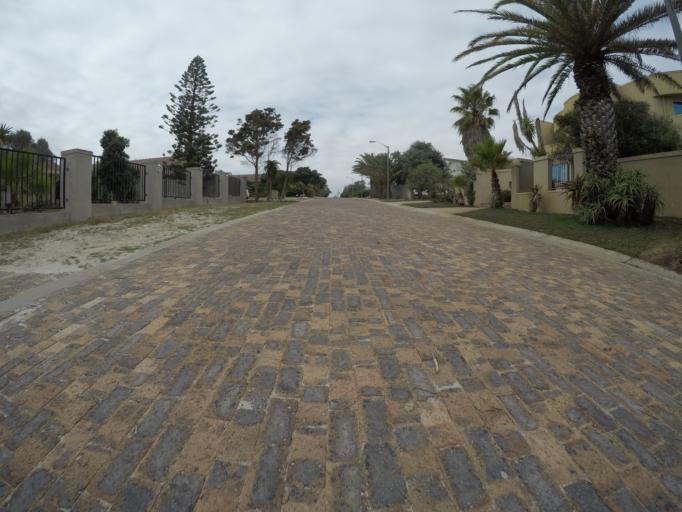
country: ZA
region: Western Cape
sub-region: City of Cape Town
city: Atlantis
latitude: -33.6930
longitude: 18.4407
